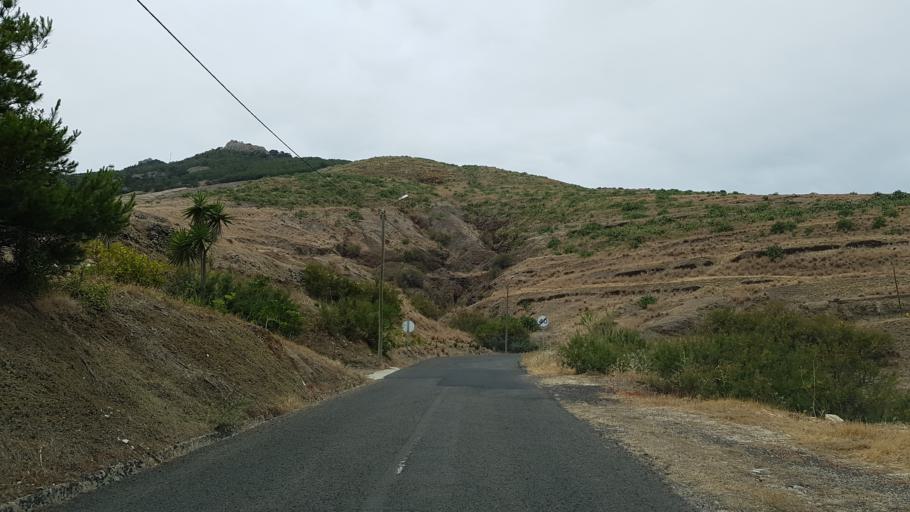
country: PT
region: Madeira
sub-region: Porto Santo
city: Vila de Porto Santo
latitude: 33.0767
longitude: -16.3124
